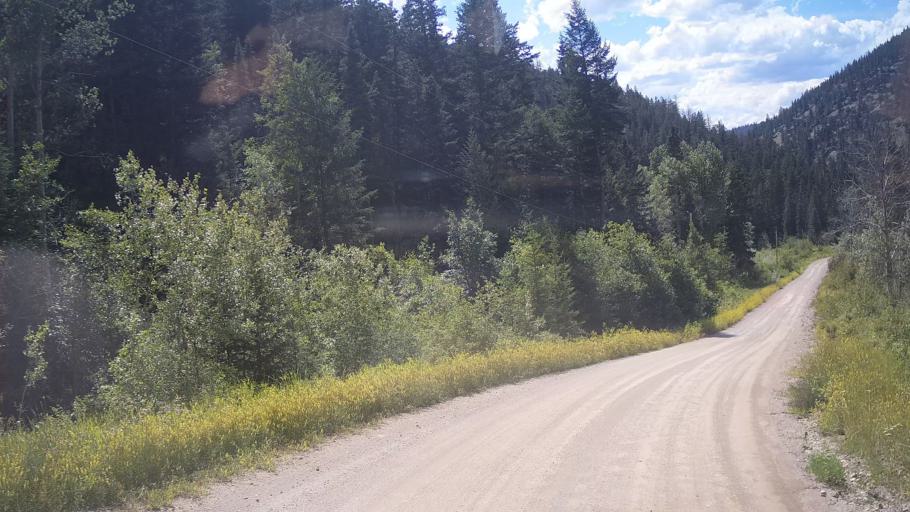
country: CA
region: British Columbia
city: Lillooet
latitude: 51.2593
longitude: -121.9882
